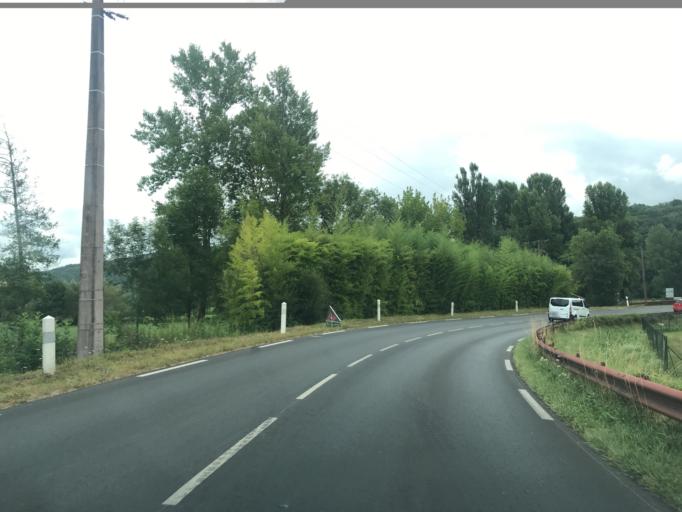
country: FR
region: Aquitaine
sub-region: Departement de la Dordogne
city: Le Bugue
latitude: 44.9544
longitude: 1.0061
